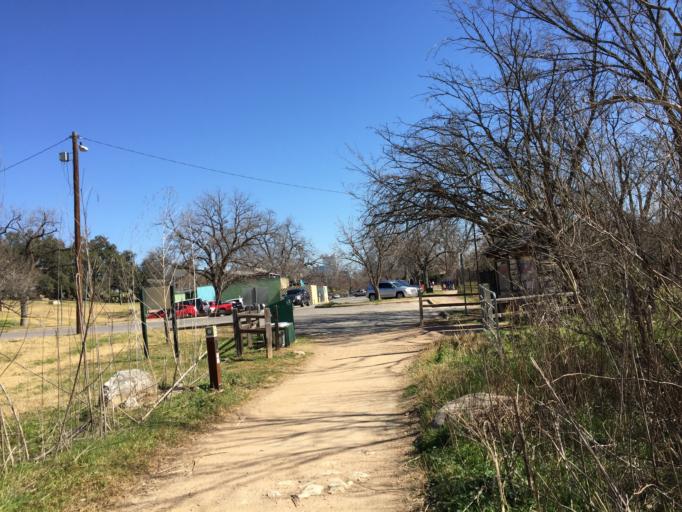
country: US
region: Texas
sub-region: Travis County
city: Rollingwood
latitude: 30.2642
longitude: -97.7735
